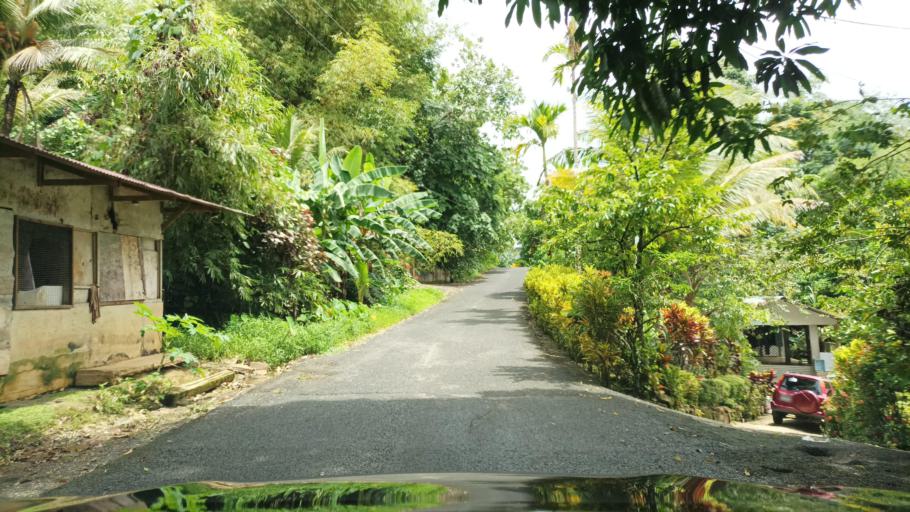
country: FM
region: Pohnpei
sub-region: Kolonia Municipality
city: Kolonia
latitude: 6.9599
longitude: 158.2252
